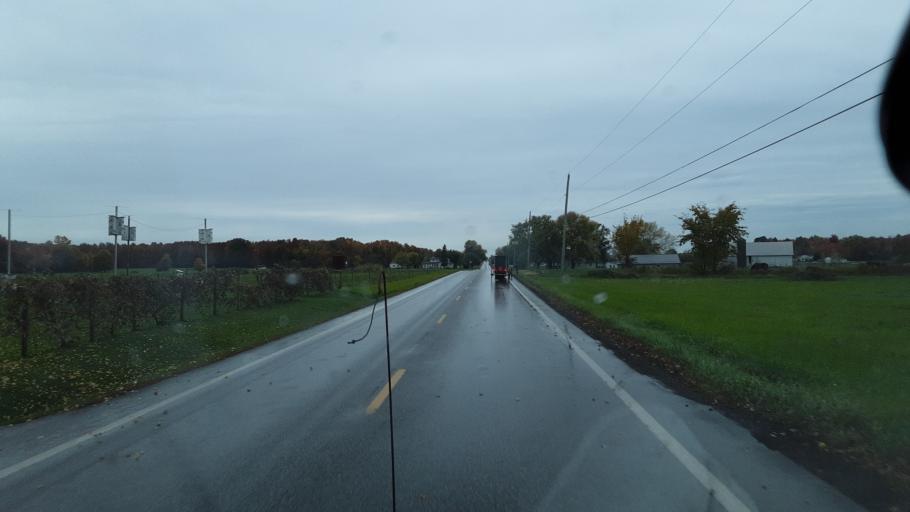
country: US
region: Ohio
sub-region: Geauga County
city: Middlefield
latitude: 41.3990
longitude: -81.0902
